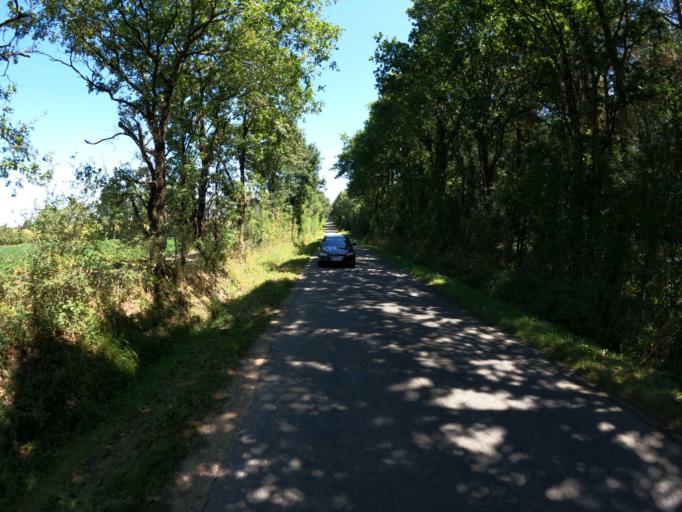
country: FR
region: Pays de la Loire
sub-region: Departement de la Loire-Atlantique
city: Lege
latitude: 46.9392
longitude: -1.6293
